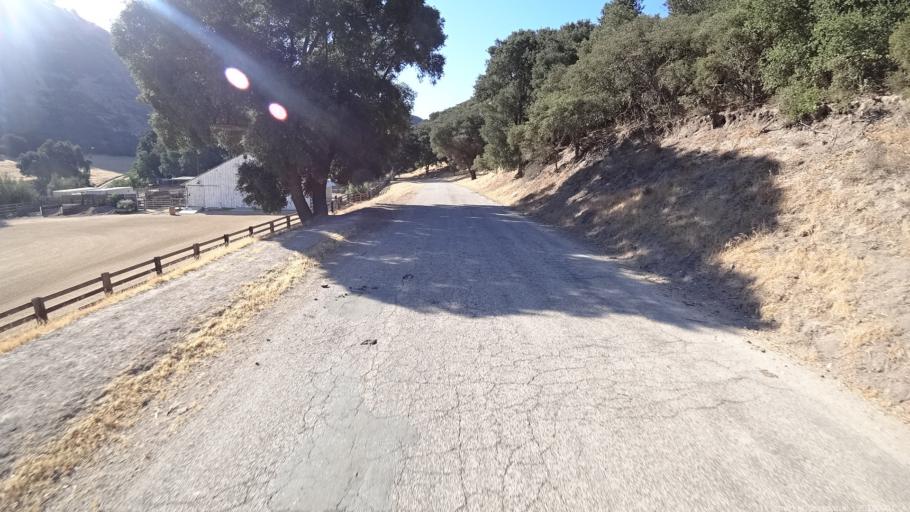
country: US
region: California
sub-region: Monterey County
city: Greenfield
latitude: 36.2052
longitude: -121.2778
